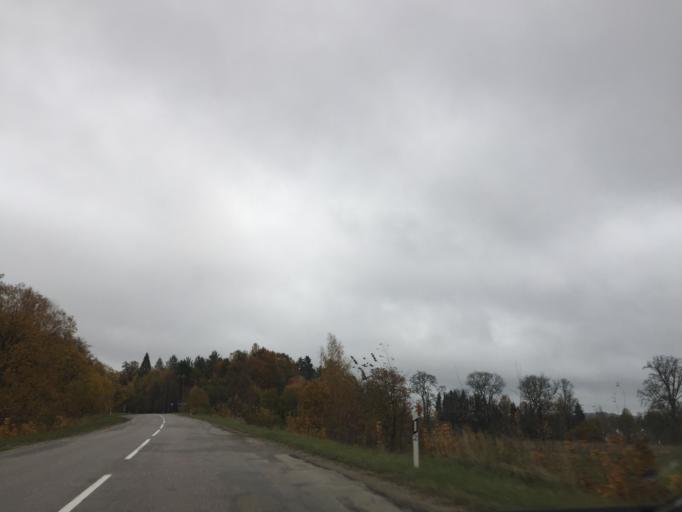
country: LV
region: Pargaujas
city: Stalbe
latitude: 57.3545
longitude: 25.0769
